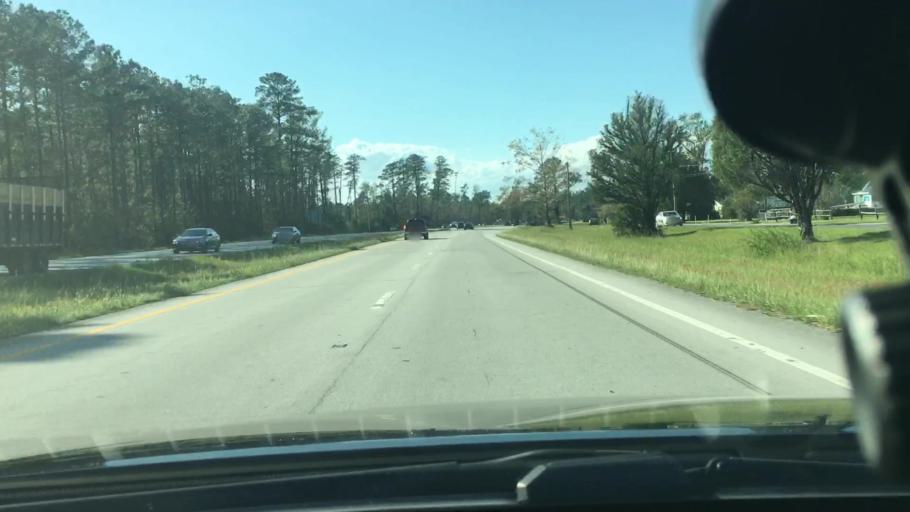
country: US
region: North Carolina
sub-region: Craven County
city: Neuse Forest
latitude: 34.9678
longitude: -76.9663
